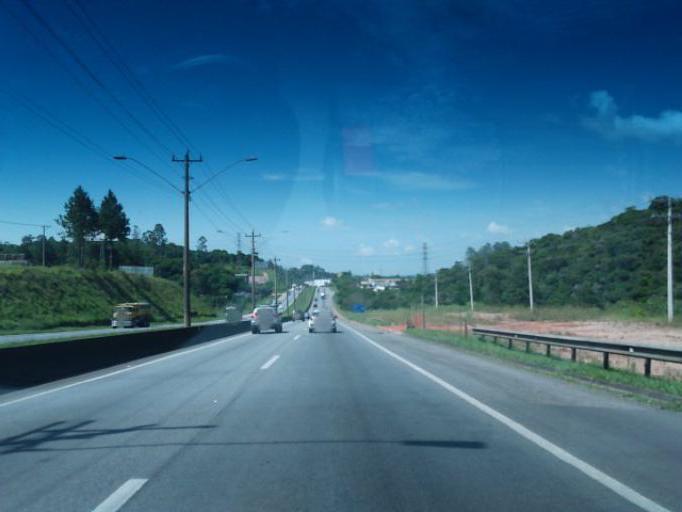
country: BR
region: Sao Paulo
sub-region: Itapecerica Da Serra
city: Itapecerica da Serra
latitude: -23.7113
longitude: -46.8775
